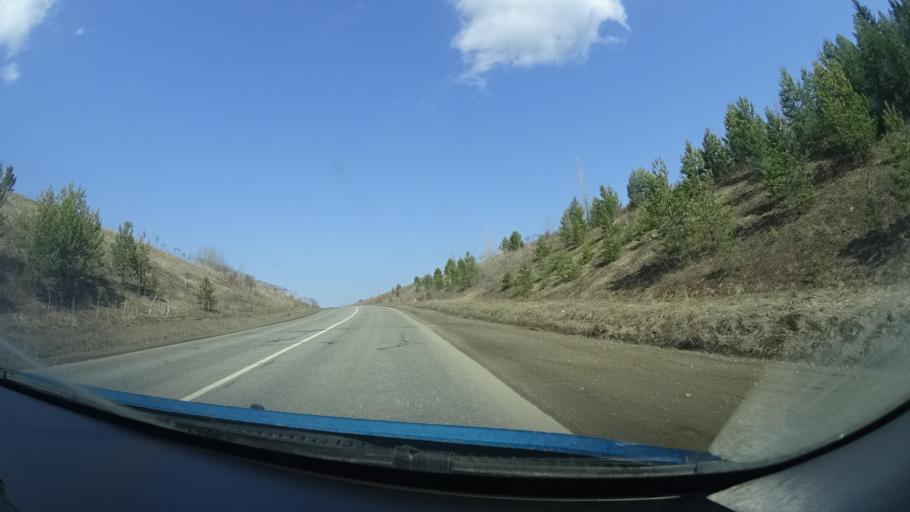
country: RU
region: Perm
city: Osa
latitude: 57.2595
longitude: 55.5754
